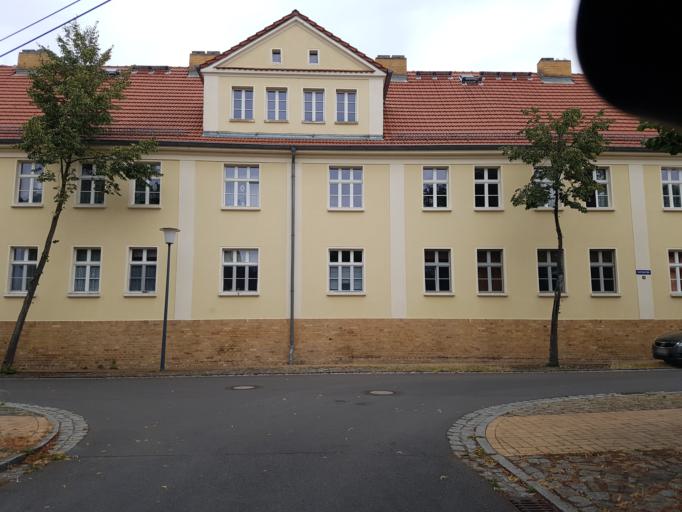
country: DE
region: Brandenburg
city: Schipkau
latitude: 51.5630
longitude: 13.8926
